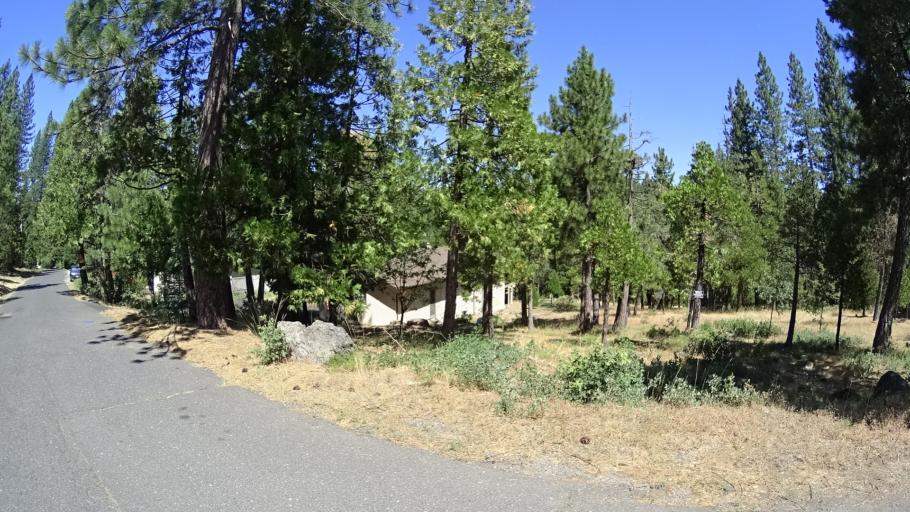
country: US
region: California
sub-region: Calaveras County
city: Arnold
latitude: 38.2339
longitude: -120.3694
